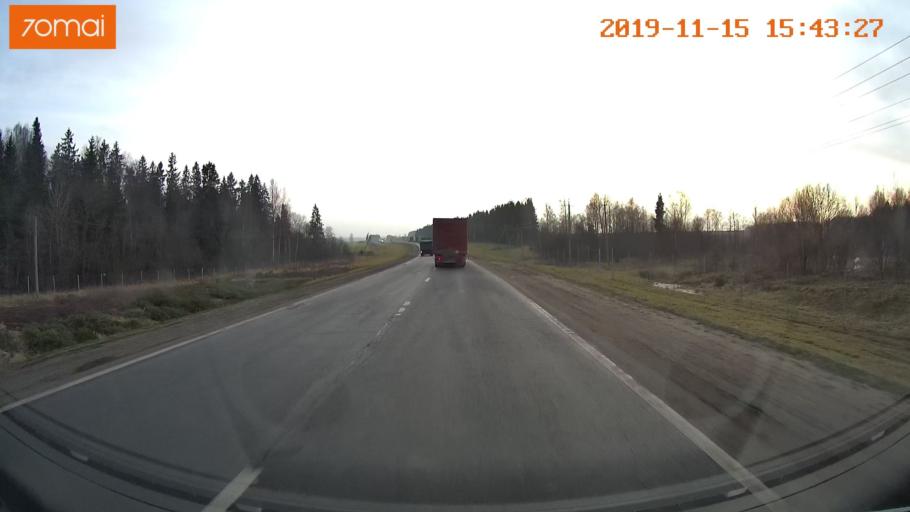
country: RU
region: Jaroslavl
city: Danilov
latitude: 57.9821
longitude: 40.0277
